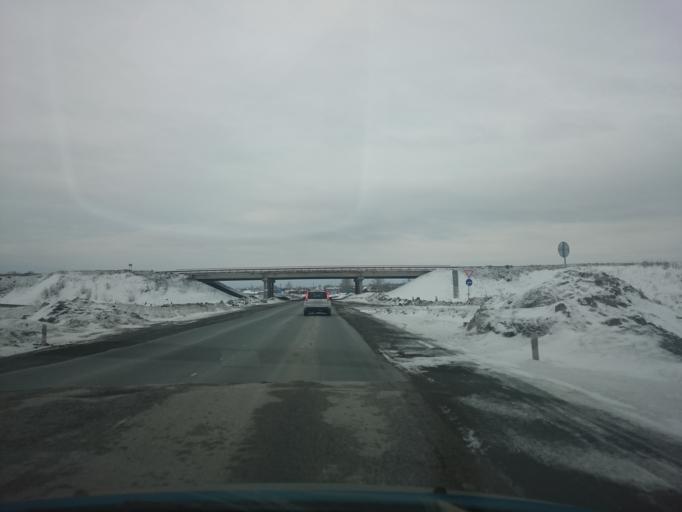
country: RU
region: Sverdlovsk
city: Achit
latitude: 56.7881
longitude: 57.8806
